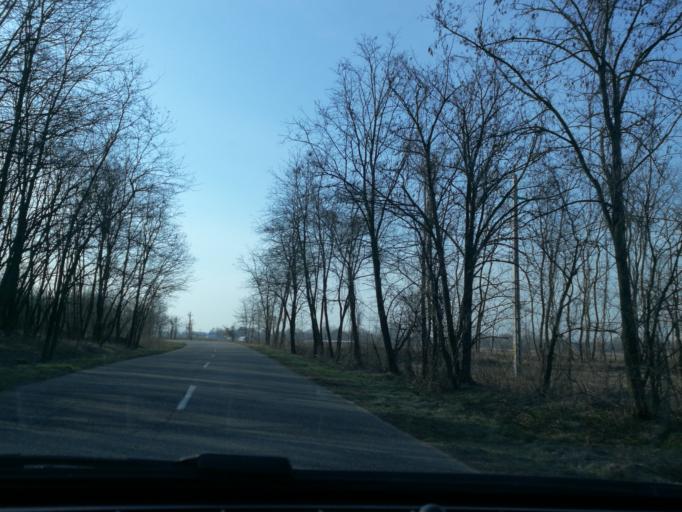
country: HU
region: Szabolcs-Szatmar-Bereg
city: Levelek
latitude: 47.9900
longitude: 21.9683
